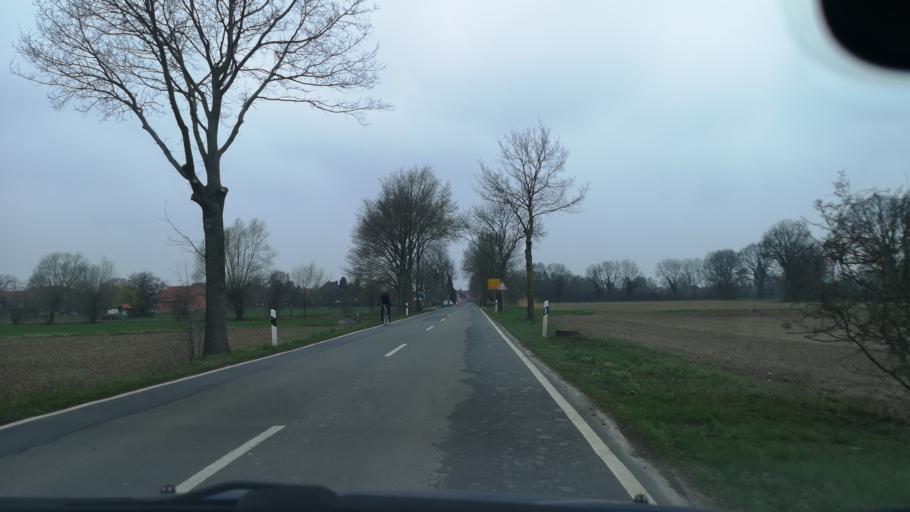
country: DE
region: Lower Saxony
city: Schwarmstedt
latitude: 52.5934
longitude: 9.5711
